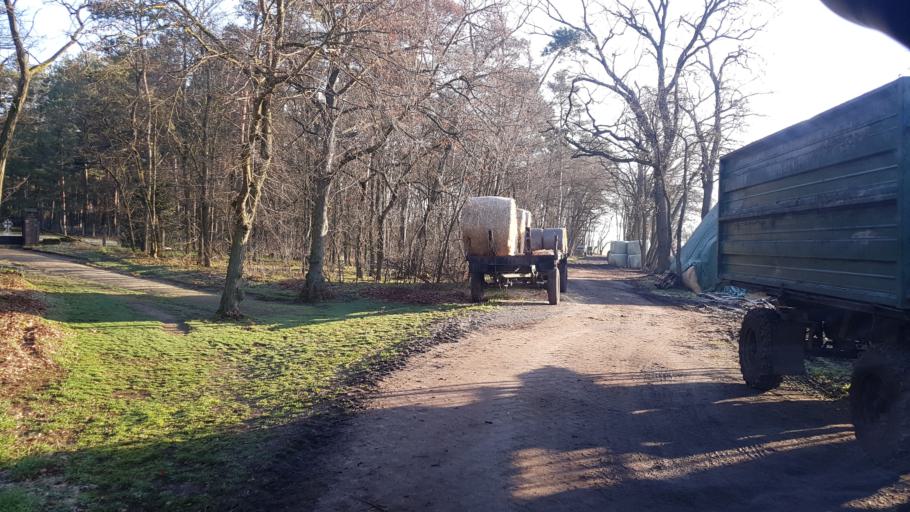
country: DE
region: Brandenburg
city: Calau
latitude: 51.7359
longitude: 13.9019
